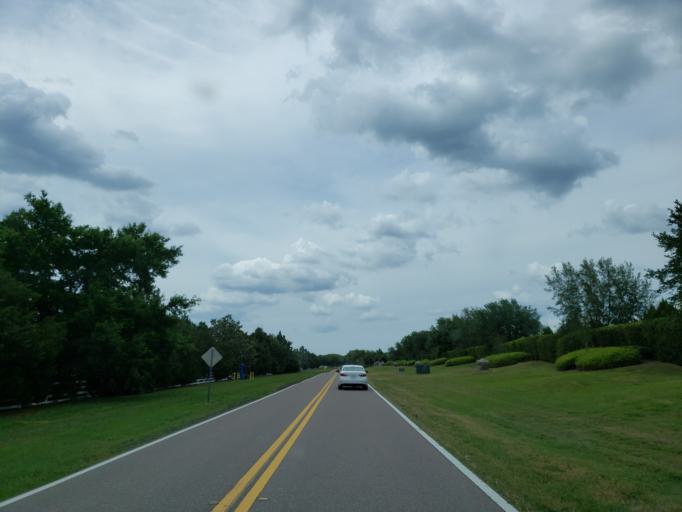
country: US
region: Florida
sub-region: Hillsborough County
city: Keystone
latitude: 28.1196
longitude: -82.6098
